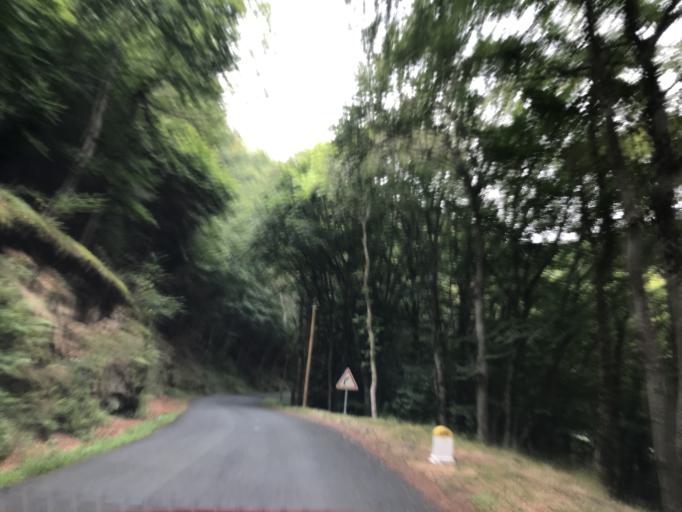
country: FR
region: Rhone-Alpes
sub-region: Departement de la Loire
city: Sail-sous-Couzan
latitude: 45.6846
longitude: 3.9027
